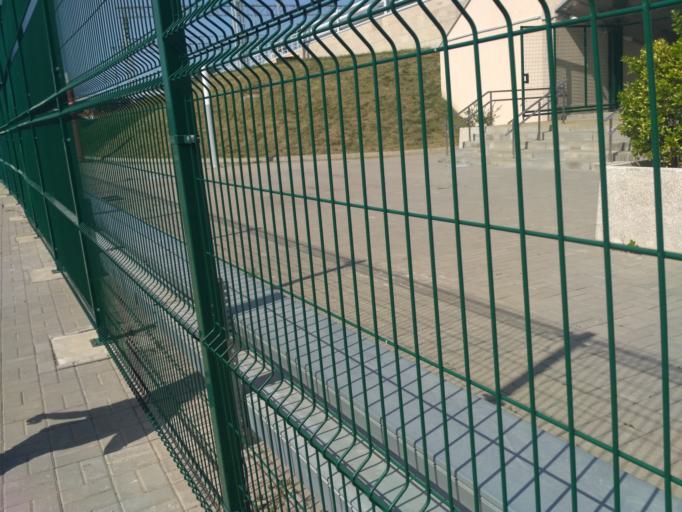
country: RU
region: Krasnodarskiy
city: Adler
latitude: 43.4123
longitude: 39.9717
